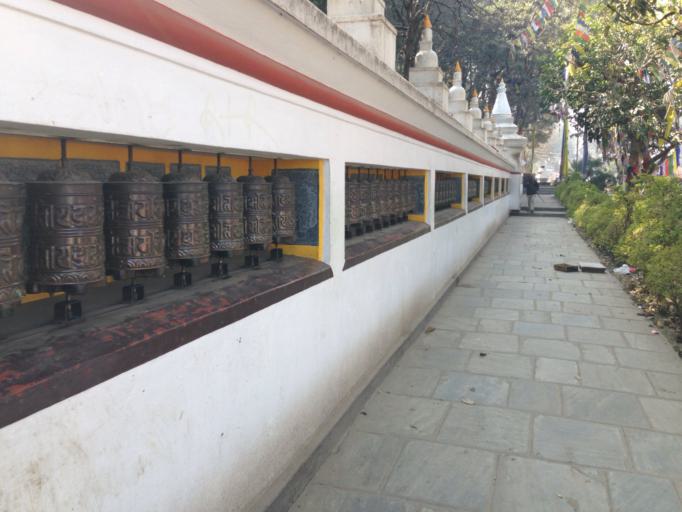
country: NP
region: Central Region
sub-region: Bagmati Zone
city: Kathmandu
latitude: 27.7176
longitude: 85.2872
